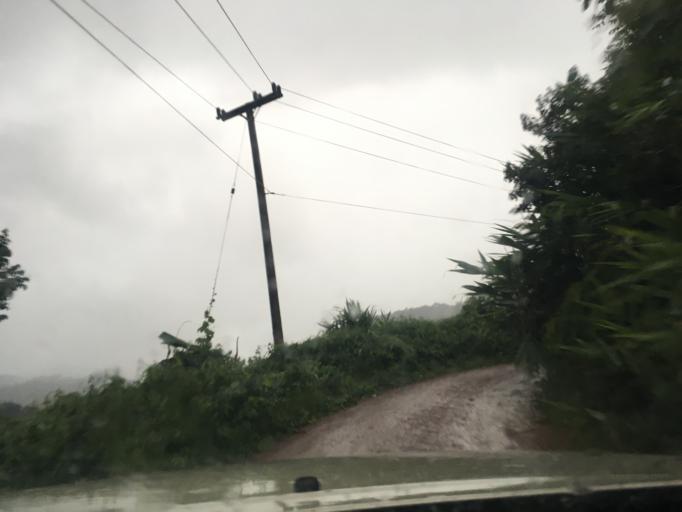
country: LA
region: Oudomxai
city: Muang La
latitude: 21.2426
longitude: 101.9431
